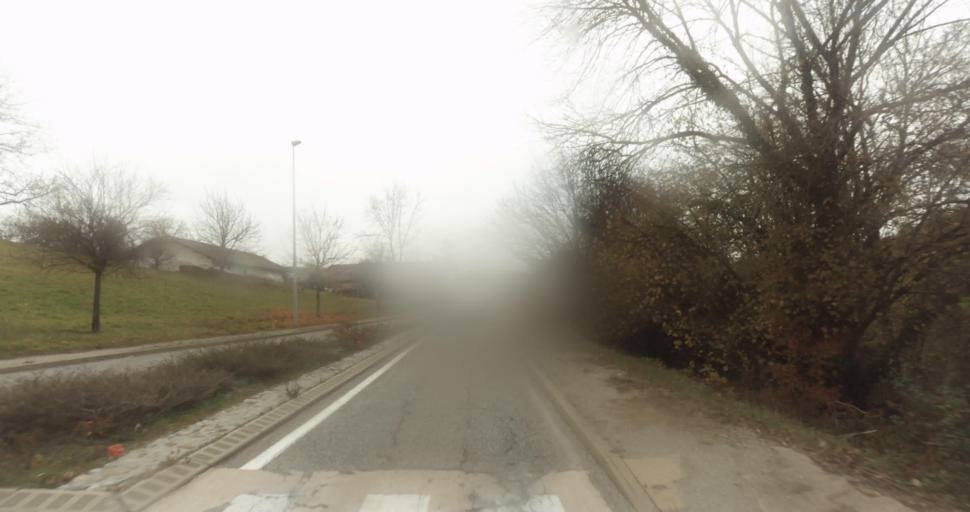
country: FR
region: Rhone-Alpes
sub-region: Departement de la Haute-Savoie
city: Saint-Martin-Bellevue
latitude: 45.9793
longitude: 6.1644
